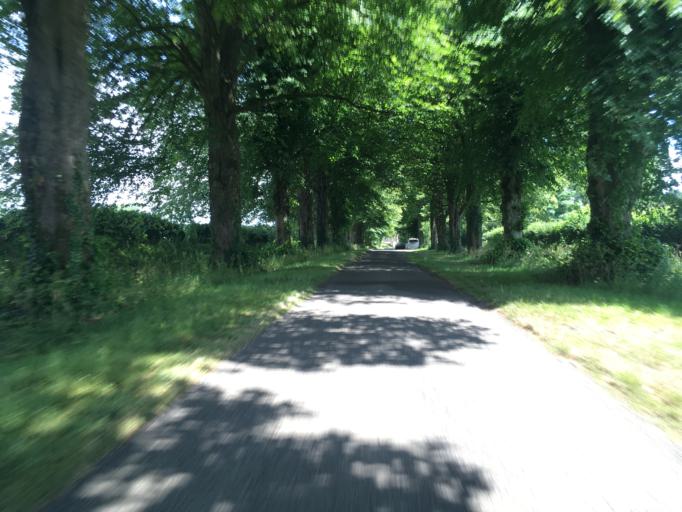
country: GB
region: England
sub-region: Gloucestershire
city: Tetbury
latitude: 51.6577
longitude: -2.1893
